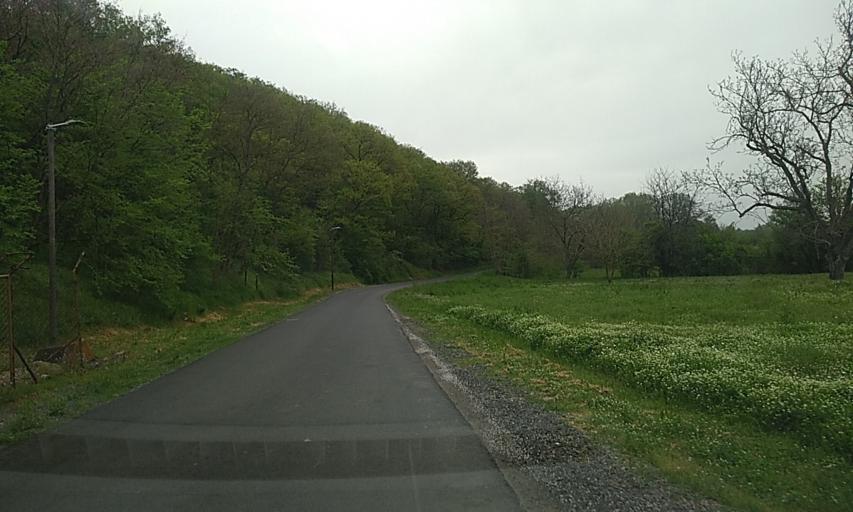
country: RS
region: Central Serbia
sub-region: Nisavski Okrug
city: Razanj
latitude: 43.6202
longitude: 21.5268
